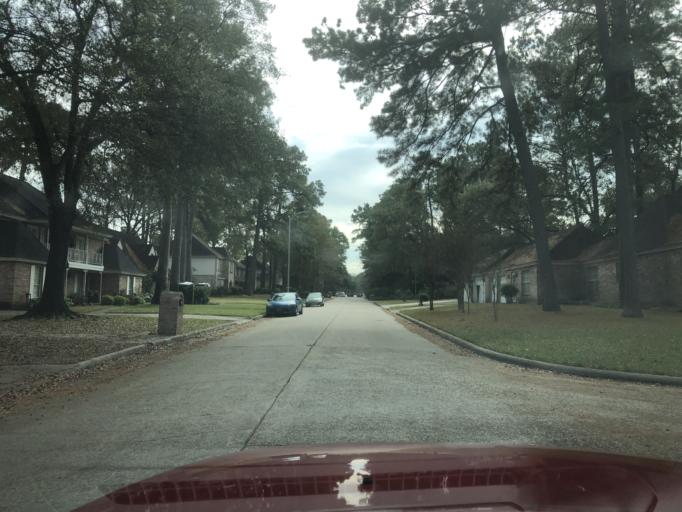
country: US
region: Texas
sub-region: Harris County
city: Spring
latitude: 30.0205
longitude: -95.4639
